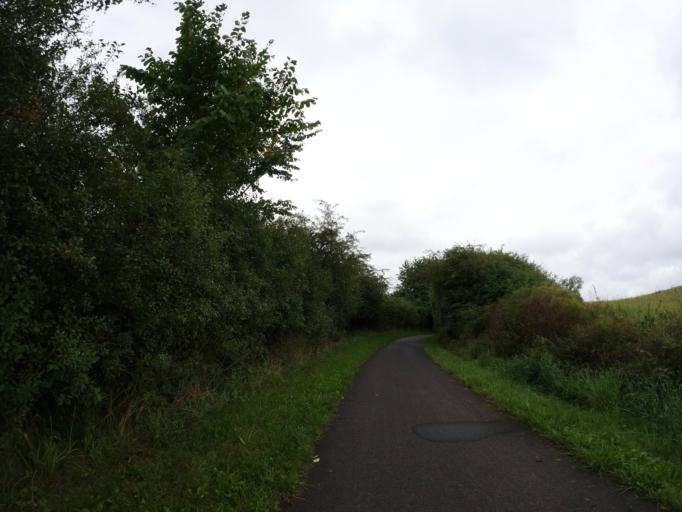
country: DE
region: Mecklenburg-Vorpommern
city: Poseritz
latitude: 54.2873
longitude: 13.2713
